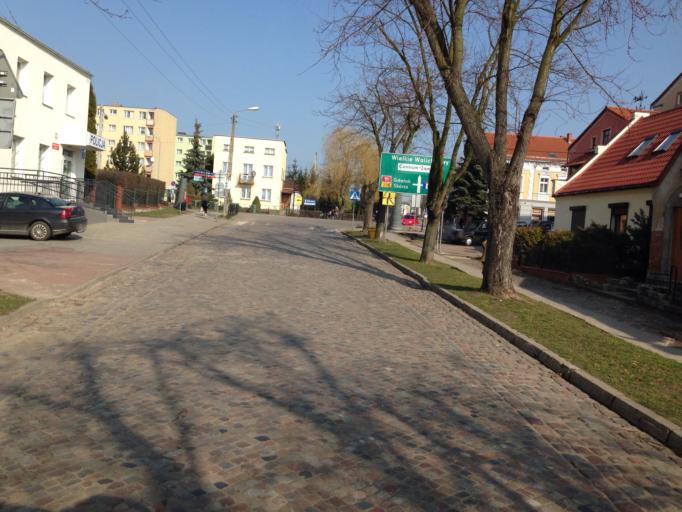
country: PL
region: Pomeranian Voivodeship
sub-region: Powiat tczewski
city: Gniew
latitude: 53.8350
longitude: 18.8217
